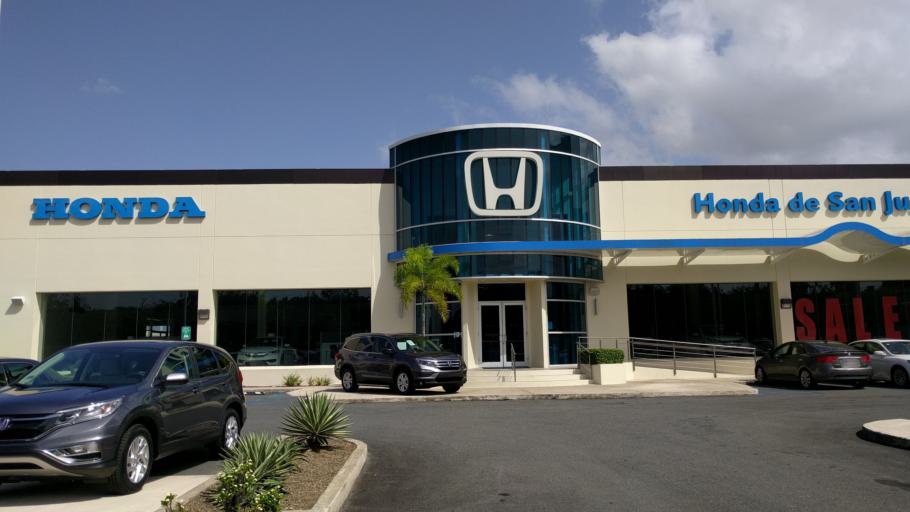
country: PR
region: Catano
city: Catano
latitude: 18.4253
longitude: -66.0951
